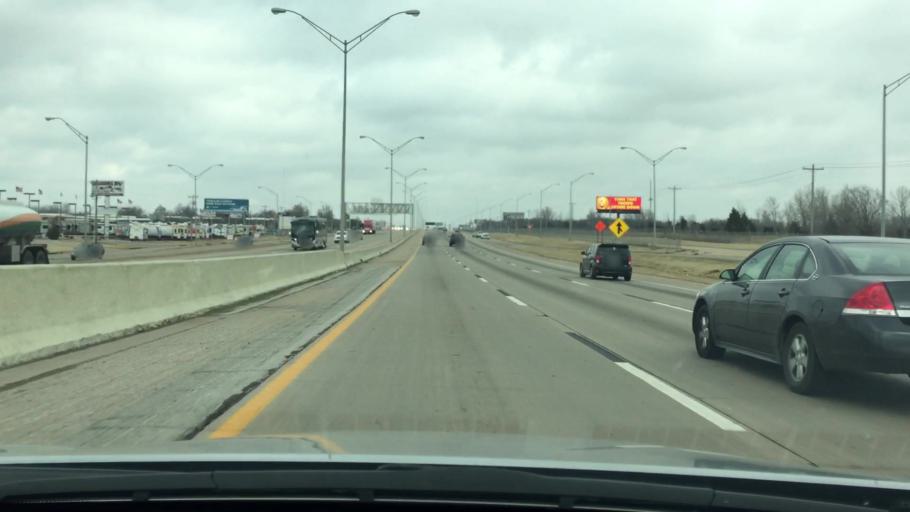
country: US
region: Oklahoma
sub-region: Cleveland County
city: Moore
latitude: 35.3652
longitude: -97.4948
